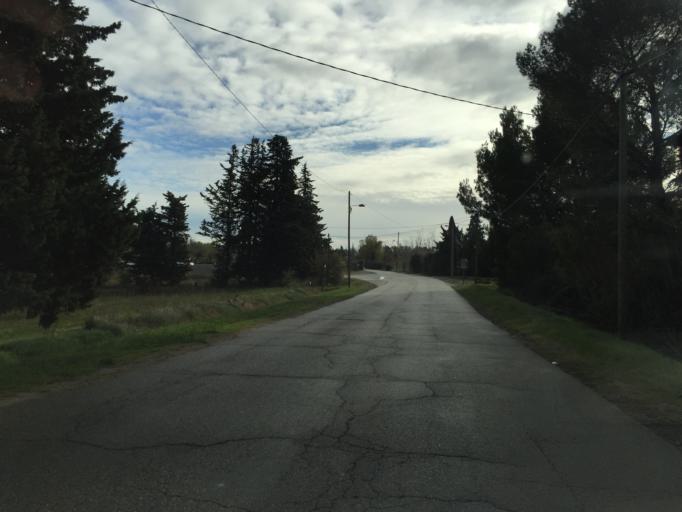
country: FR
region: Provence-Alpes-Cote d'Azur
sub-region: Departement du Vaucluse
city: Sorgues
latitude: 43.9987
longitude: 4.8895
